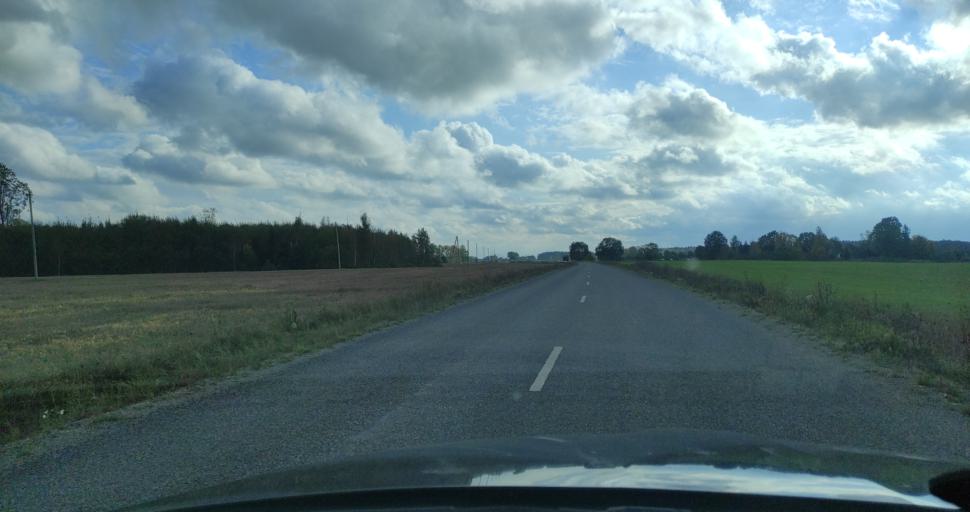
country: LV
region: Talsu Rajons
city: Sabile
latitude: 56.9283
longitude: 22.3955
